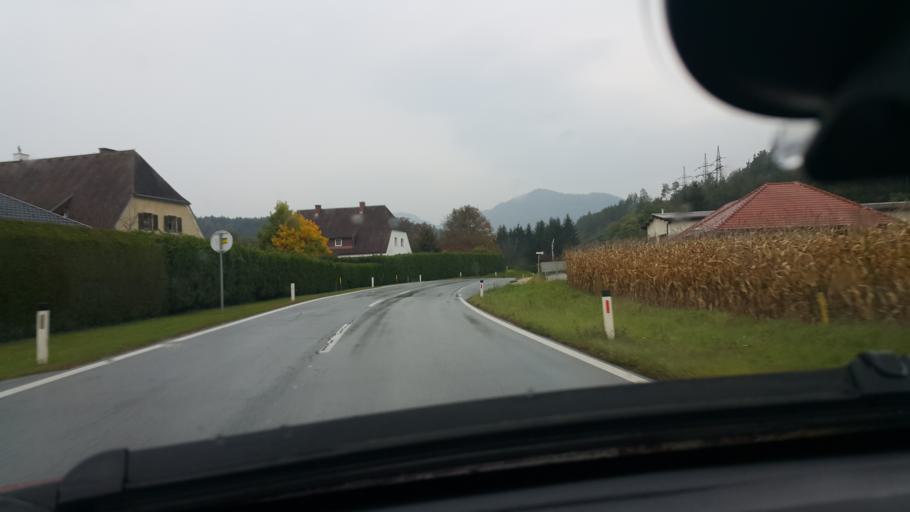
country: AT
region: Carinthia
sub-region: Politischer Bezirk Volkermarkt
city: Neuhaus
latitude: 46.6569
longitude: 14.8791
